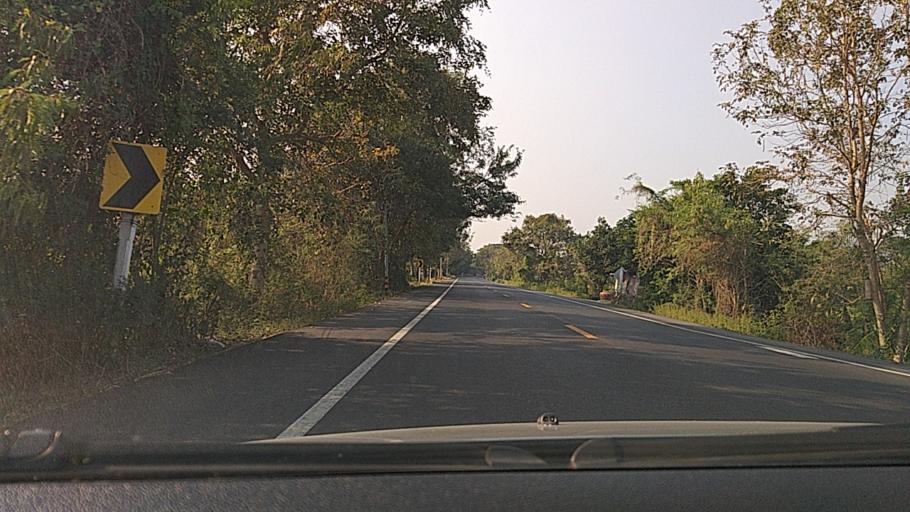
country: TH
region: Sing Buri
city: Phrom Buri
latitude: 14.7534
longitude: 100.4379
